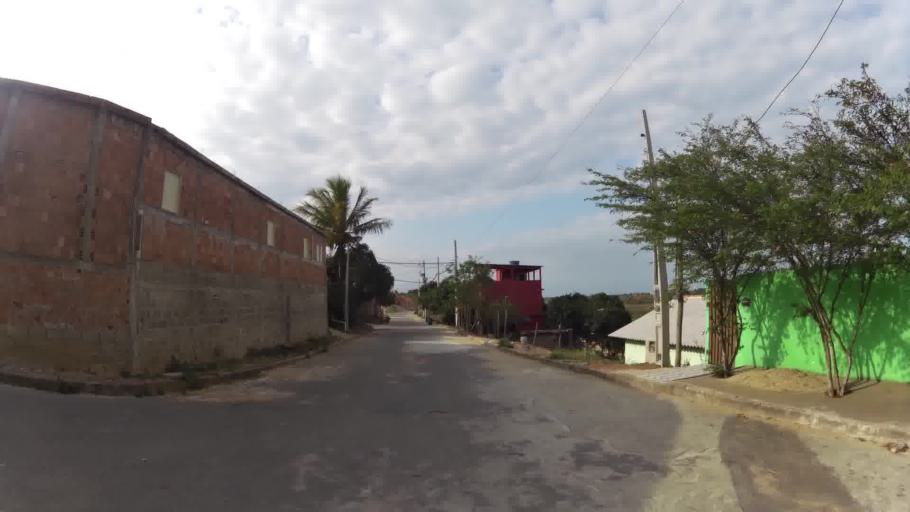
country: BR
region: Espirito Santo
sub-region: Itapemirim
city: Itapemirim
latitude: -21.0166
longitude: -40.8283
